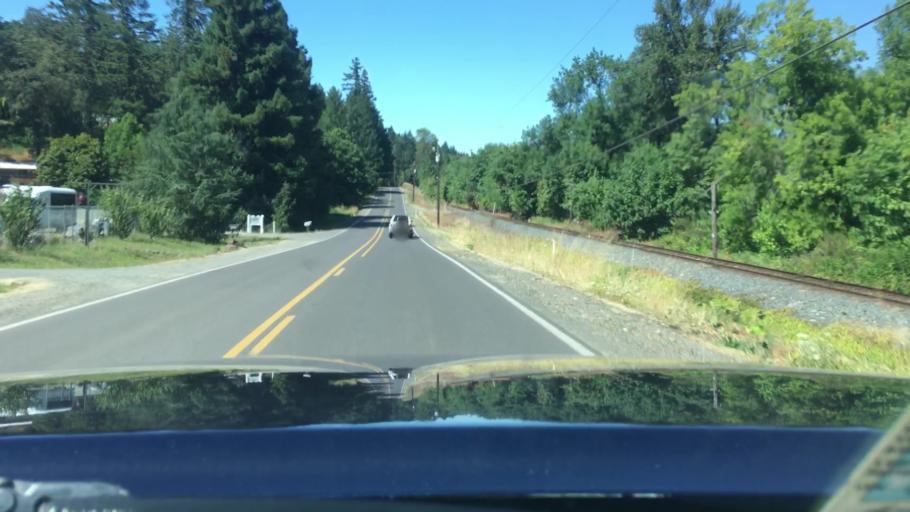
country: US
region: Oregon
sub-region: Lane County
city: Cottage Grove
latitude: 43.8155
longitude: -123.0457
